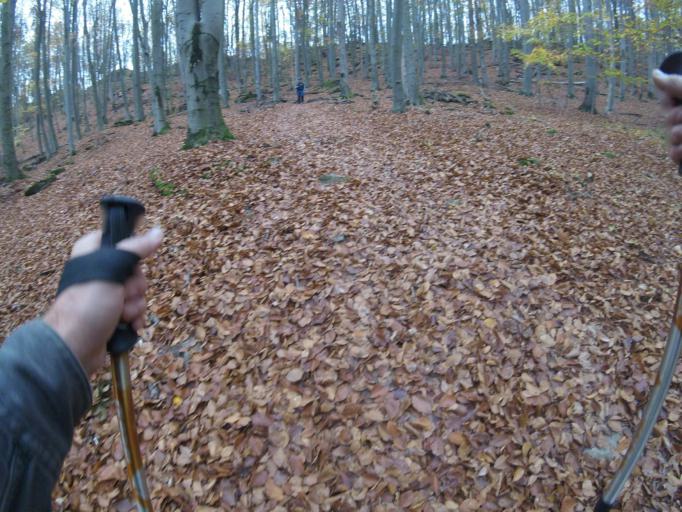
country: HU
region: Borsod-Abauj-Zemplen
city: Tolcsva
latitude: 48.3996
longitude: 21.4052
